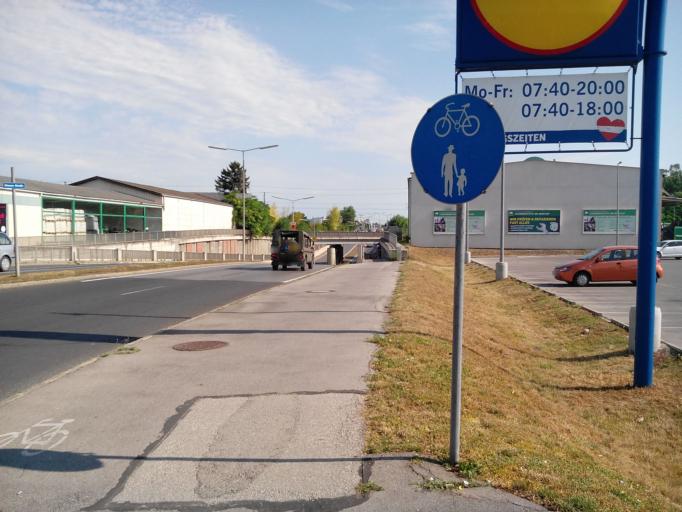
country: AT
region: Lower Austria
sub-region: Politischer Bezirk Wiener Neustadt
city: Theresienfeld
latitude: 47.8297
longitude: 16.2445
